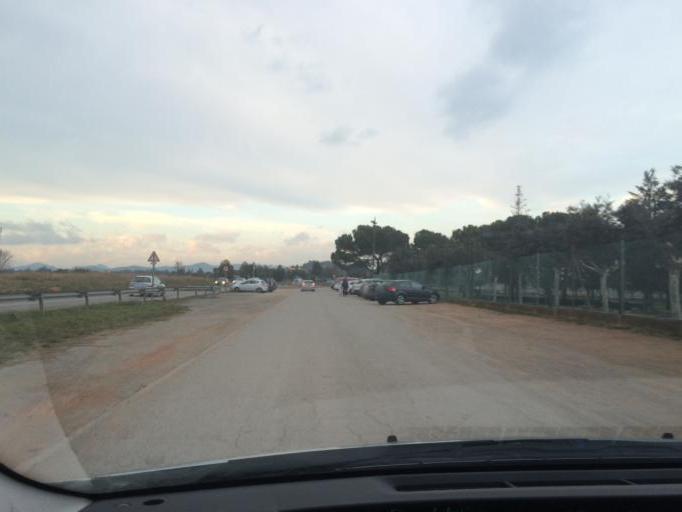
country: ES
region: Catalonia
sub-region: Provincia de Barcelona
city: Sant Fruitos de Bages
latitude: 41.7489
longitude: 1.8408
